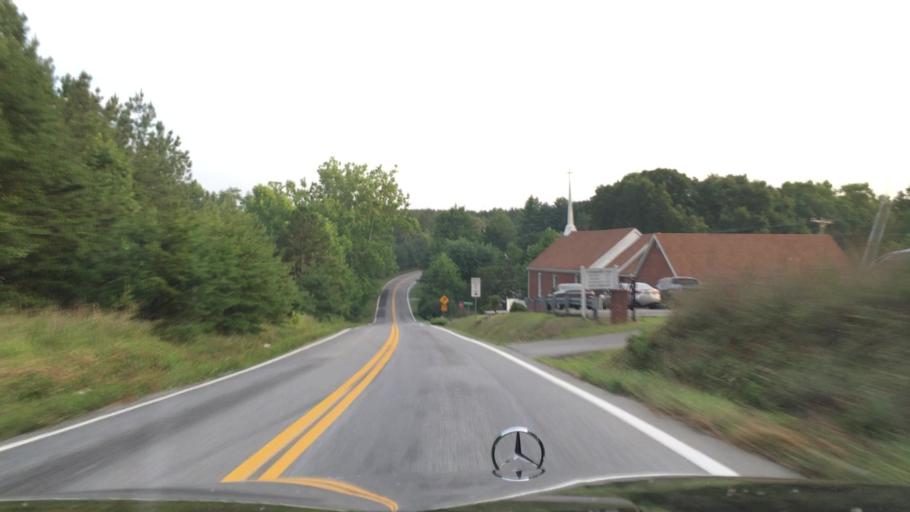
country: US
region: Virginia
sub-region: Campbell County
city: Timberlake
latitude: 37.2667
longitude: -79.2639
